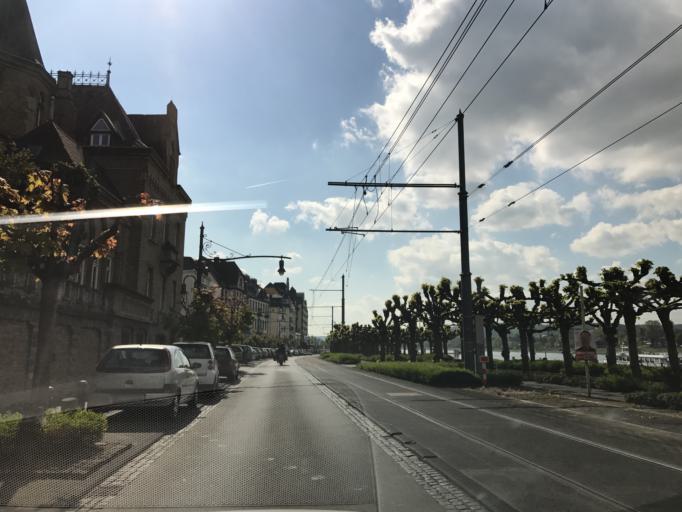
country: DE
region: North Rhine-Westphalia
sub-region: Regierungsbezirk Koln
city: Konigswinter
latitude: 50.6762
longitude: 7.1899
